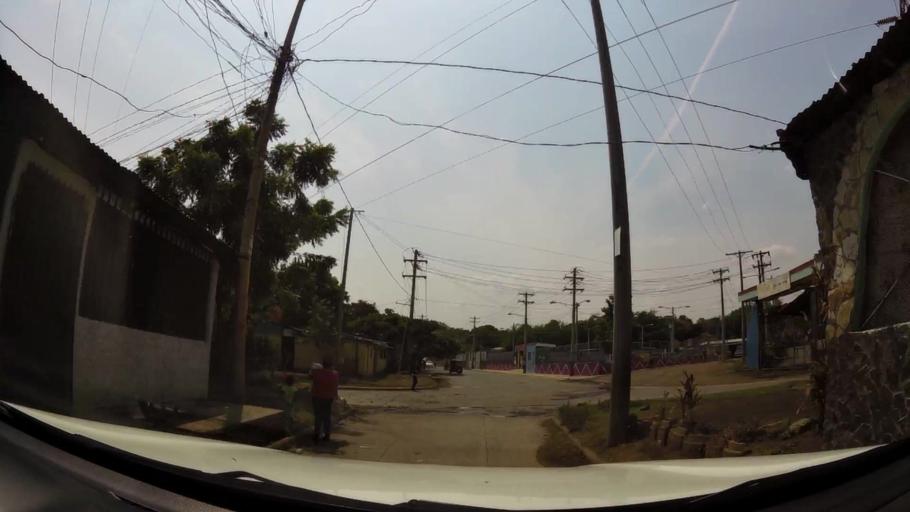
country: NI
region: Managua
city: Ciudad Sandino
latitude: 12.1596
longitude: -86.3109
